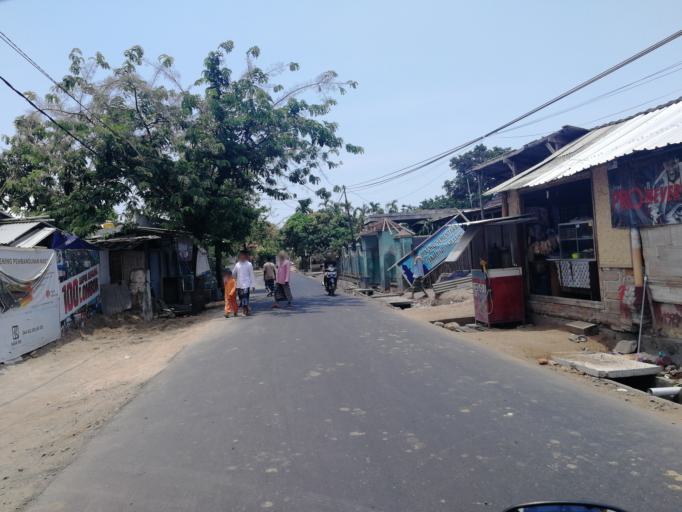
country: ID
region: West Nusa Tenggara
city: Pemenang
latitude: -8.4019
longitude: 116.1018
